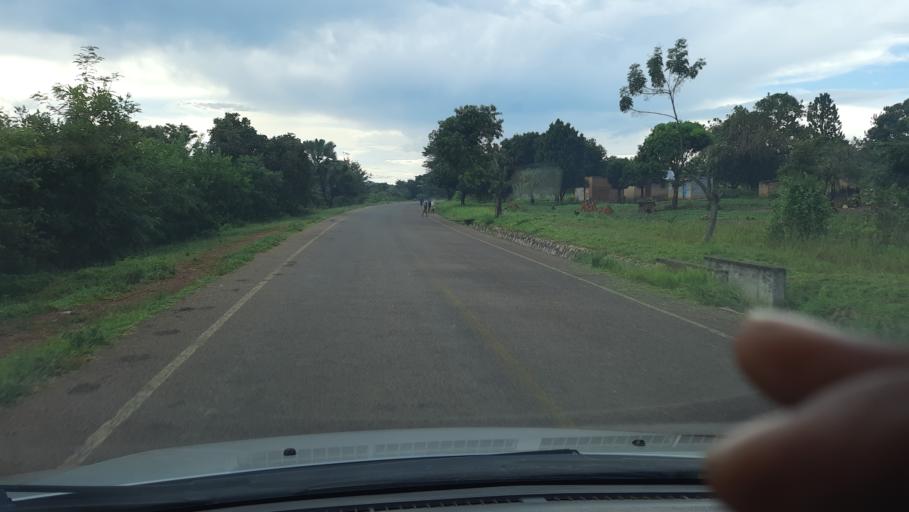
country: UG
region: Central Region
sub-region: Nakasongola District
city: Nakasongola
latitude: 1.3148
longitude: 32.4415
